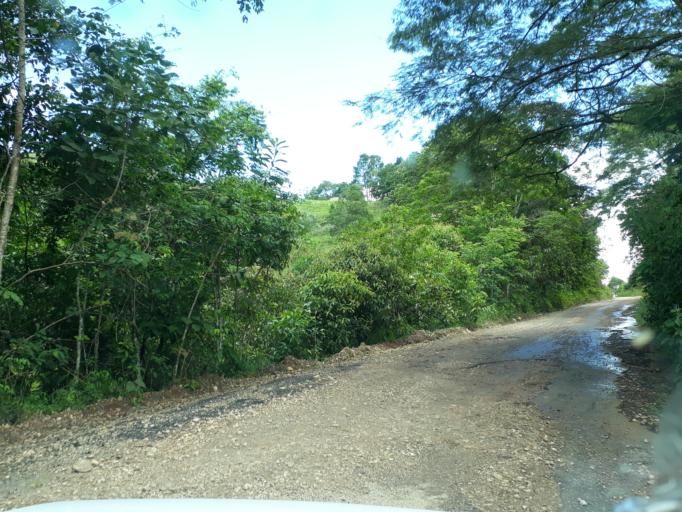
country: CO
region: Cundinamarca
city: Medina
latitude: 4.5874
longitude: -73.3133
